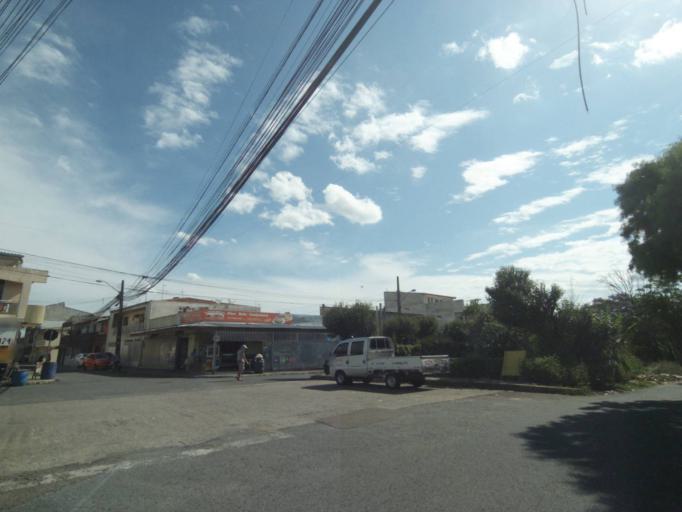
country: BR
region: Parana
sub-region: Curitiba
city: Curitiba
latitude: -25.5162
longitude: -49.3286
